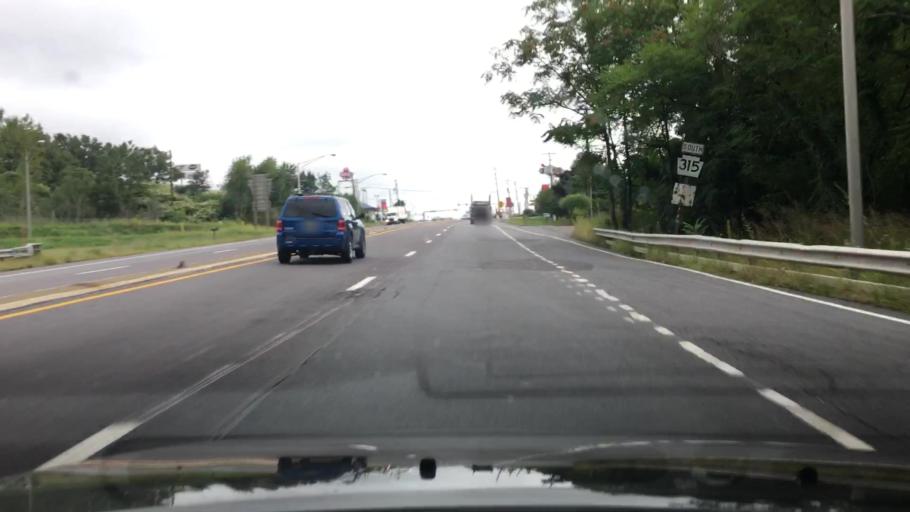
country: US
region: Pennsylvania
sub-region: Luzerne County
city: Hughestown
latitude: 41.3086
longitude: -75.7619
